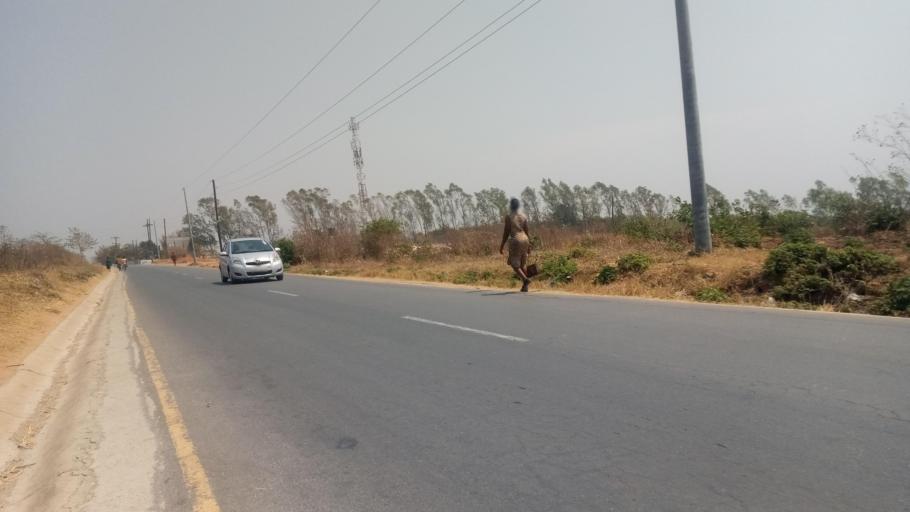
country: ZM
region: Lusaka
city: Lusaka
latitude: -15.4324
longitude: 28.3752
